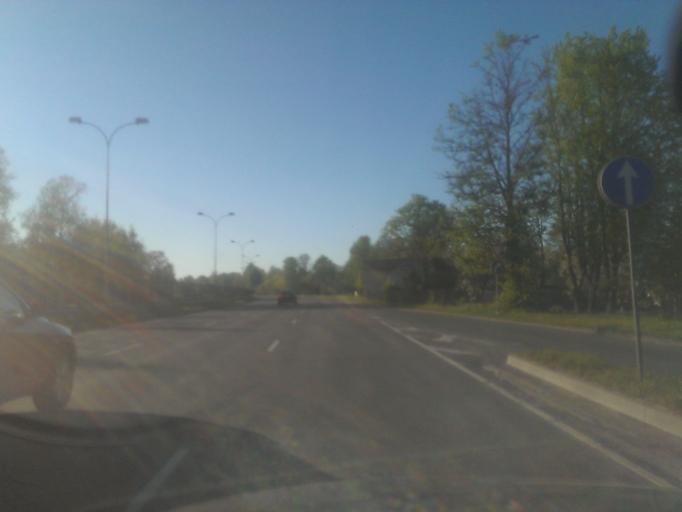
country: LV
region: Marupe
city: Marupe
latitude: 56.9444
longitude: 23.9956
